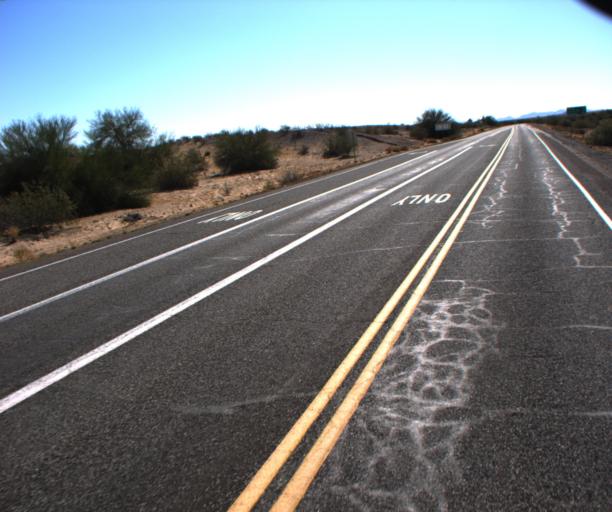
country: US
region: Arizona
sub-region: La Paz County
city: Parker
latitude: 33.9945
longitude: -114.2159
